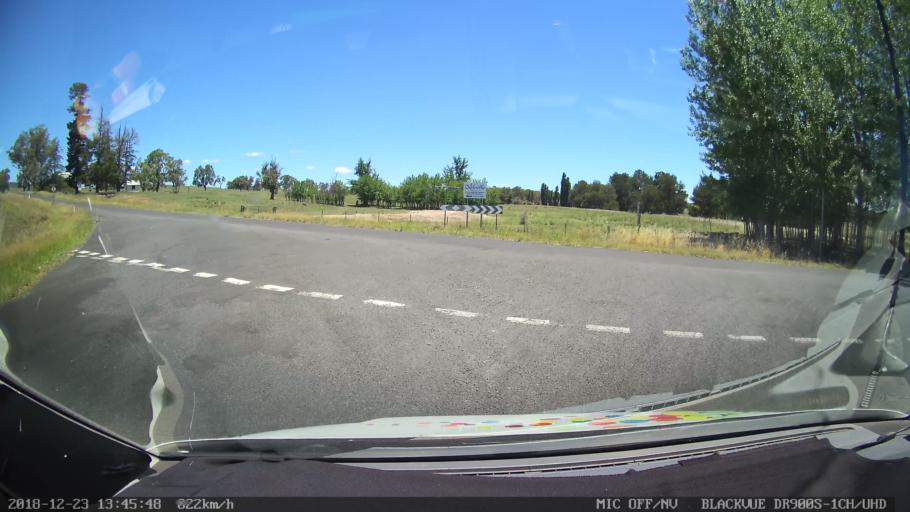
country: AU
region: New South Wales
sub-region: Tamworth Municipality
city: Manilla
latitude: -30.5043
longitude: 151.1237
